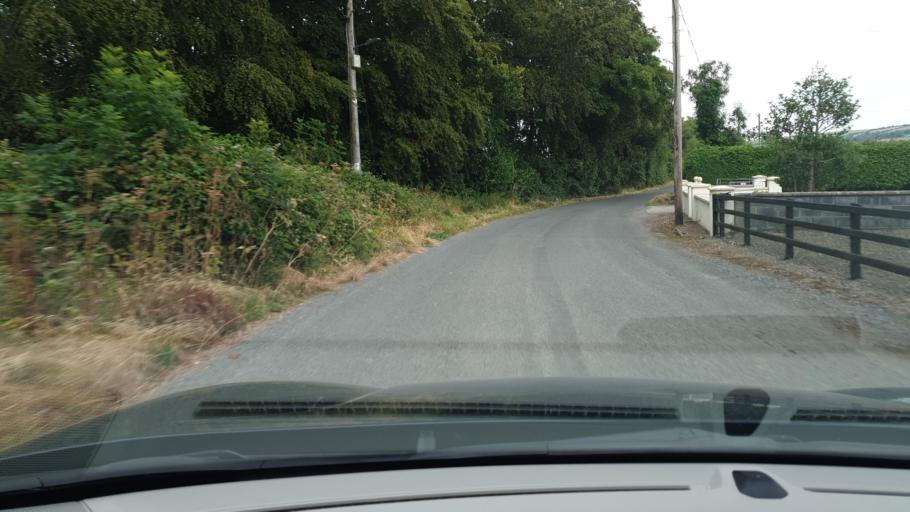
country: IE
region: Leinster
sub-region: An Mhi
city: Stamullin
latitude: 53.5953
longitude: -6.2624
